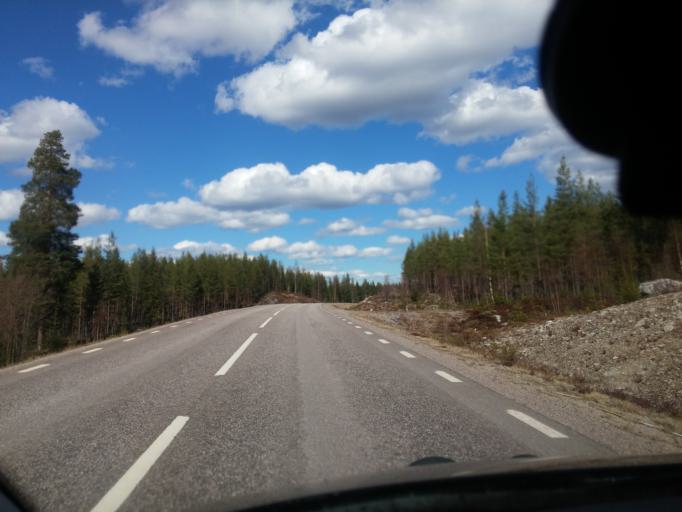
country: SE
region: Gaevleborg
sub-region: Ovanakers Kommun
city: Edsbyn
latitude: 61.2444
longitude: 15.8840
